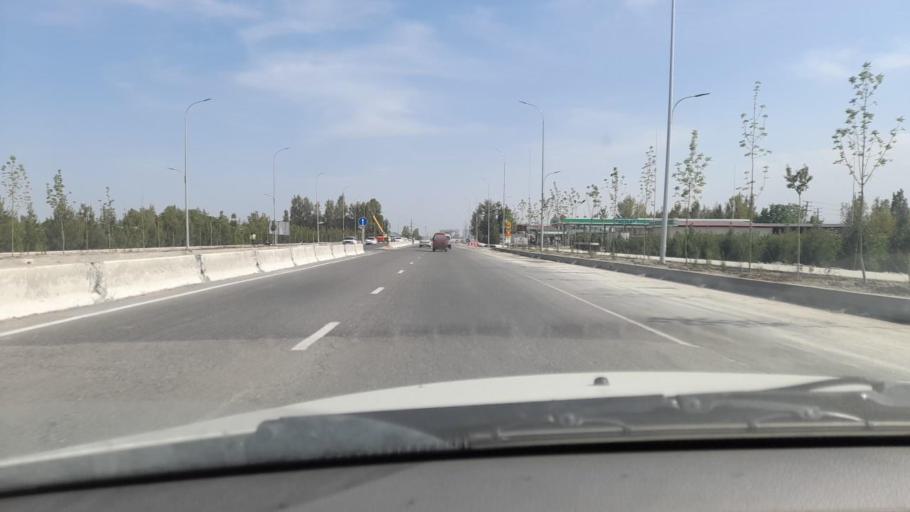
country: UZ
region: Samarqand
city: Daxbet
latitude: 39.7472
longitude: 66.9228
